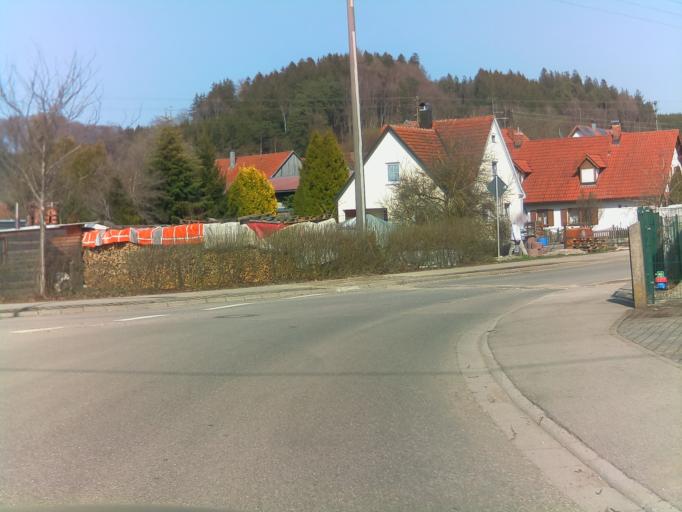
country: DE
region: Bavaria
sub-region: Swabia
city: Waltenhausen
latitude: 48.1899
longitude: 10.3609
